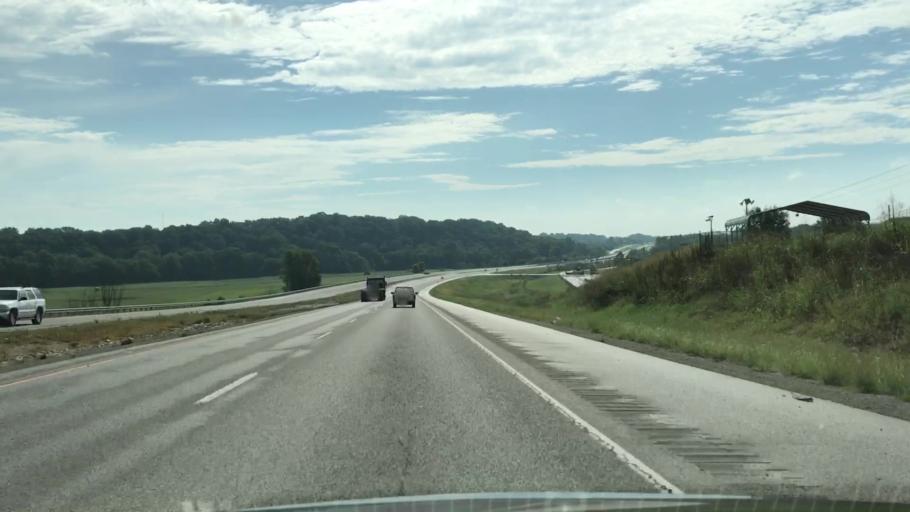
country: US
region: Kentucky
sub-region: Warren County
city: Plano
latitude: 36.9008
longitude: -86.3902
